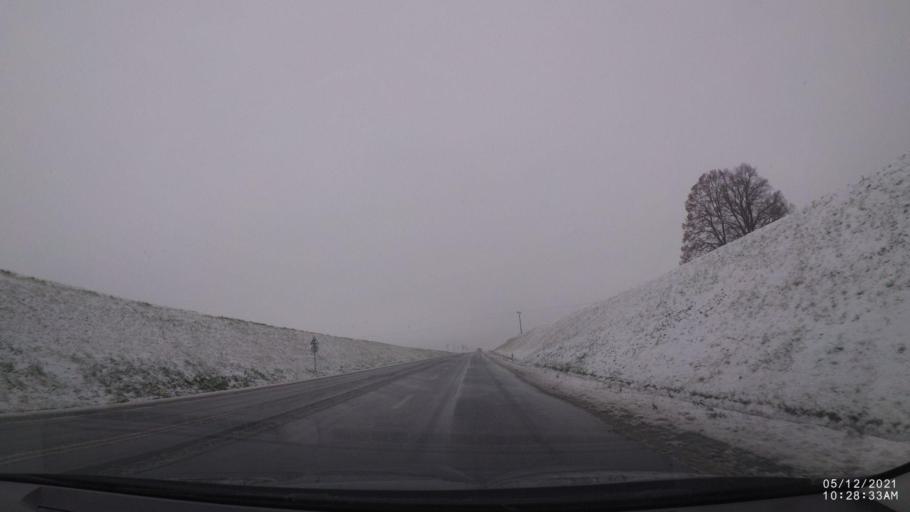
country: CZ
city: Vamberk
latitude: 50.1234
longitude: 16.2834
